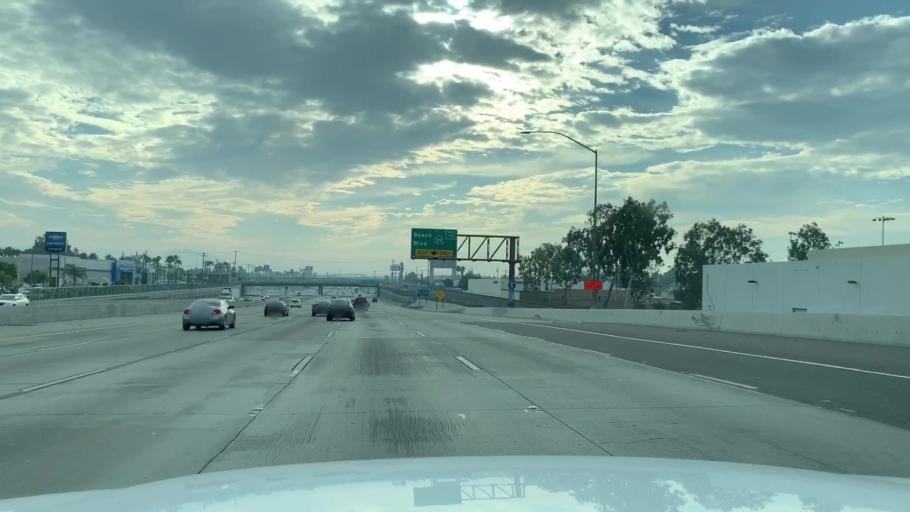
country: US
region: California
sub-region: Orange County
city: Buena Park
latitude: 33.8708
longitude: -118.0067
